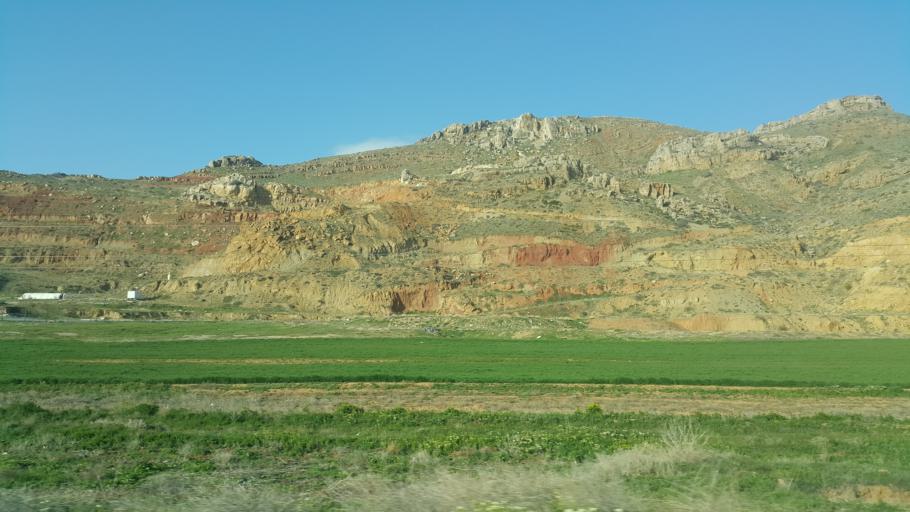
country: TR
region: Ankara
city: Sereflikochisar
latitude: 38.9851
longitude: 33.4831
